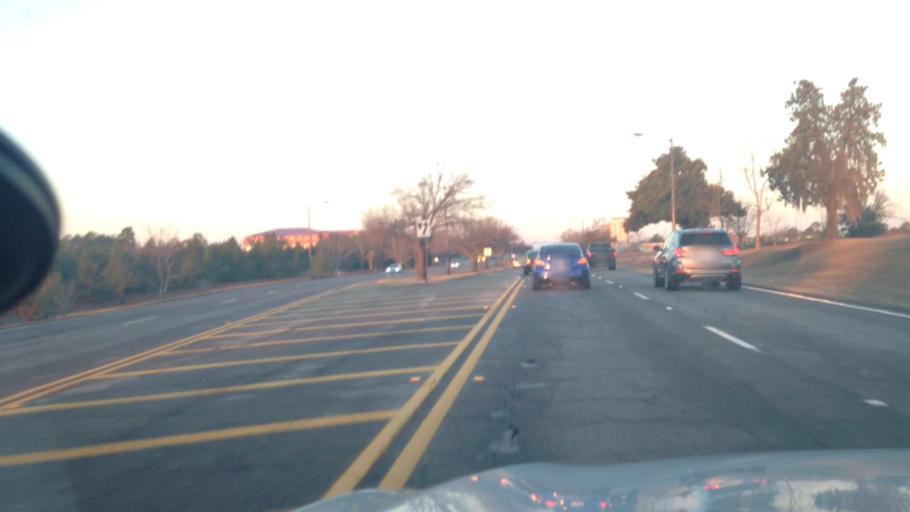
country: US
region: Georgia
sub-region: Columbia County
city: Grovetown
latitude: 33.4252
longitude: -82.1309
